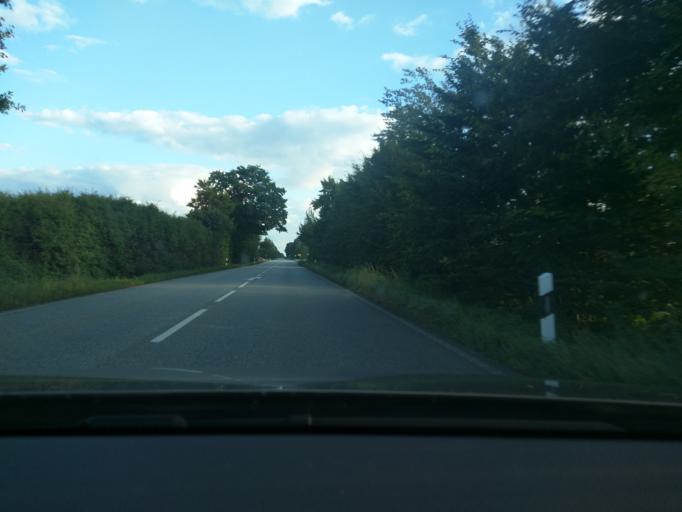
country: DE
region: Schleswig-Holstein
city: Schulendorf
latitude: 53.4751
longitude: 10.5336
